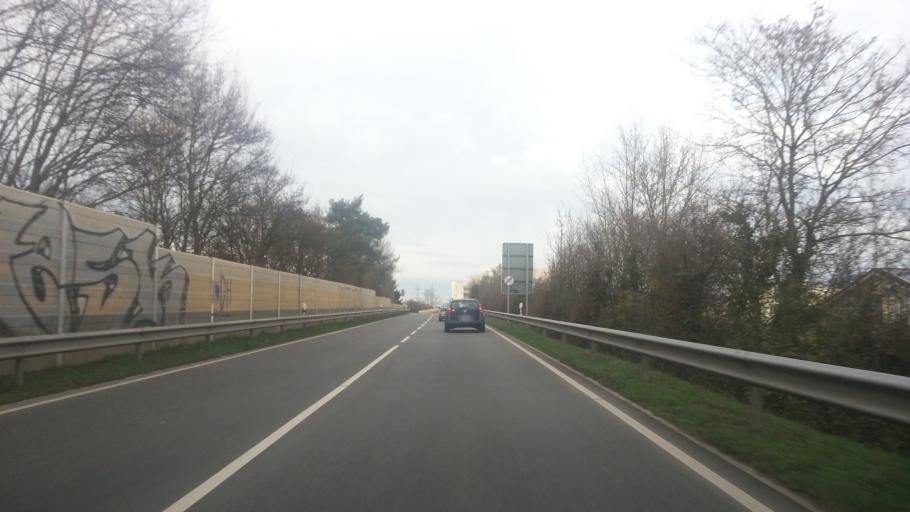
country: DE
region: Baden-Wuerttemberg
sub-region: Karlsruhe Region
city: Sandhausen
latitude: 49.3396
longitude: 8.6661
